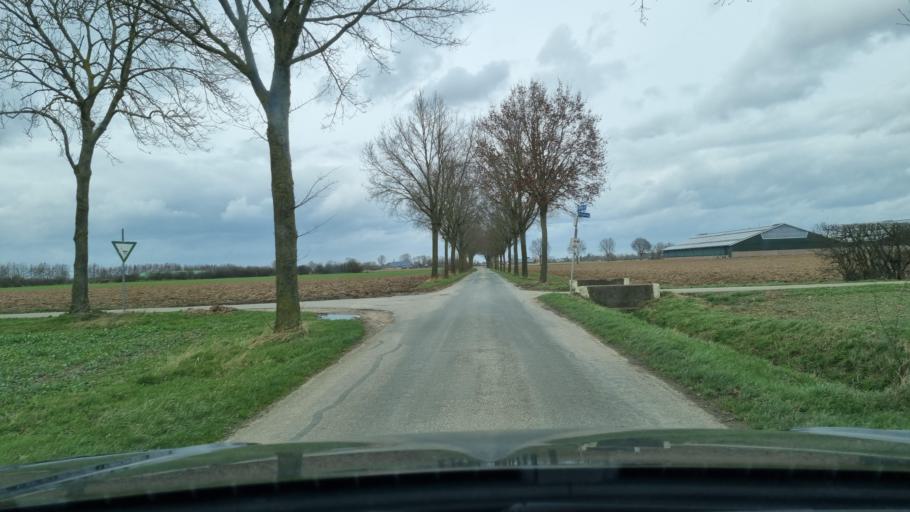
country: DE
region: North Rhine-Westphalia
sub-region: Regierungsbezirk Dusseldorf
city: Kranenburg
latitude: 51.8311
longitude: 6.0735
